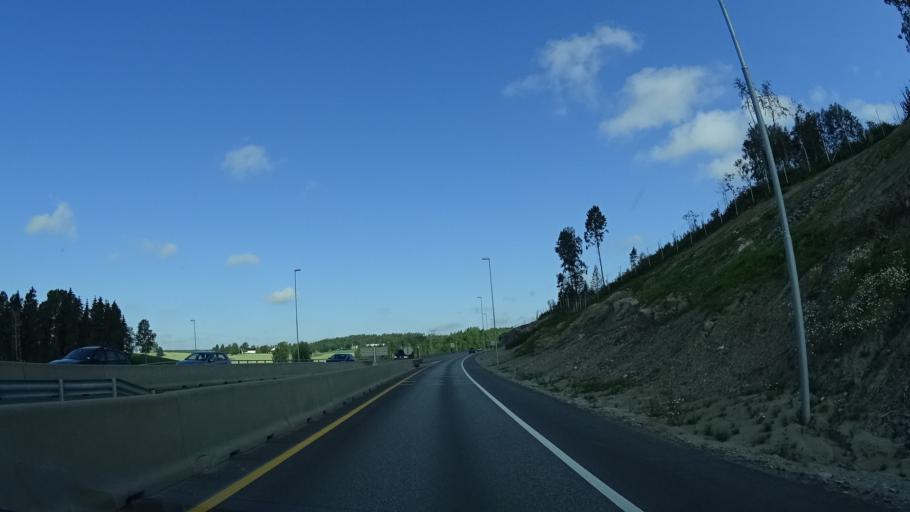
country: NO
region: Ostfold
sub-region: Hobol
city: Elvestad
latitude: 59.6443
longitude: 10.9277
